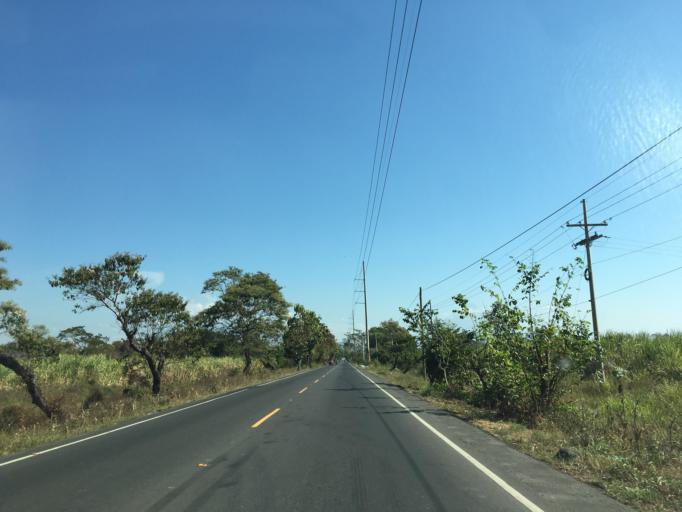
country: GT
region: Escuintla
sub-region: Municipio de La Democracia
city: La Democracia
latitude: 14.2154
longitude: -90.9545
